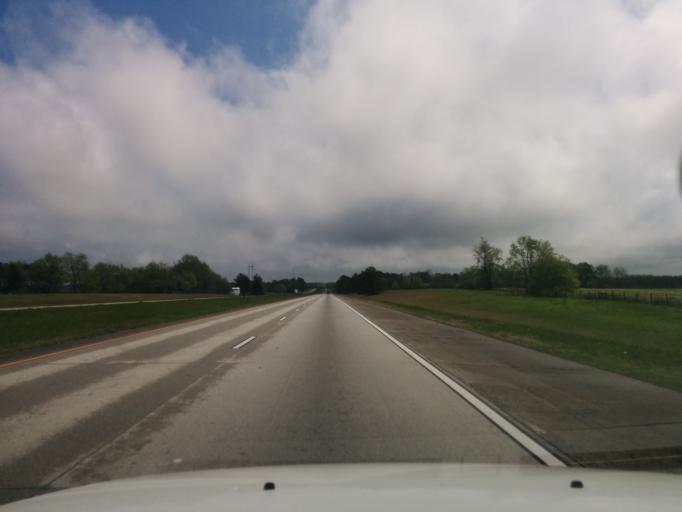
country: US
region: Georgia
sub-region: Candler County
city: Metter
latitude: 32.3581
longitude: -81.9941
